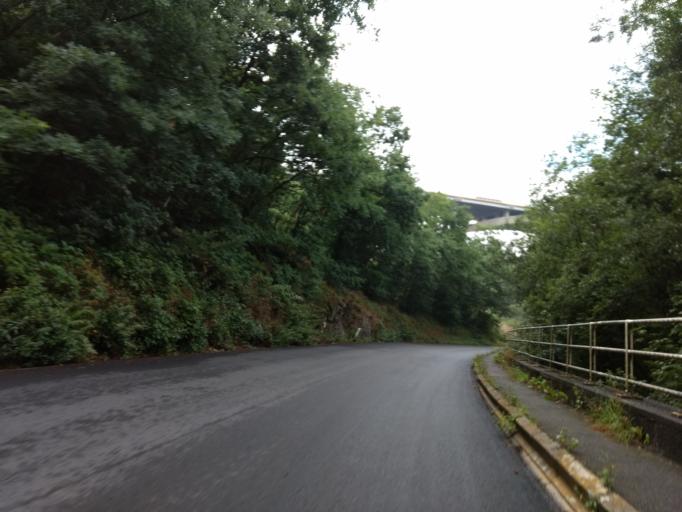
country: BE
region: Wallonia
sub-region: Province du Luxembourg
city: Houffalize
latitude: 50.1337
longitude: 5.7670
